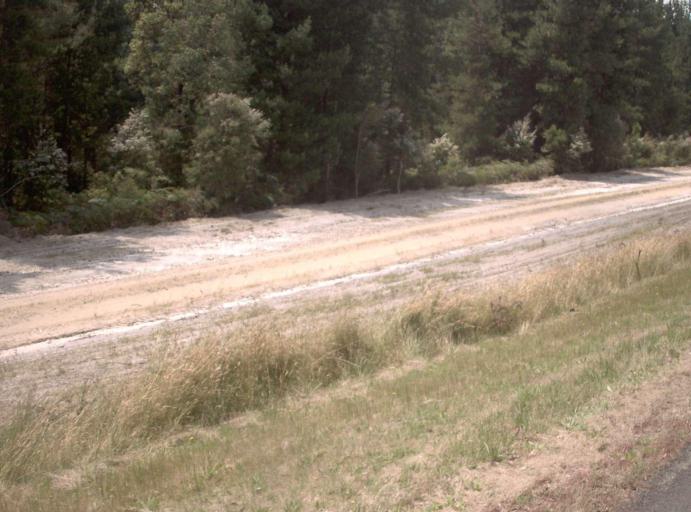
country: AU
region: Victoria
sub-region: Latrobe
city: Traralgon
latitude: -38.2595
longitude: 146.6791
